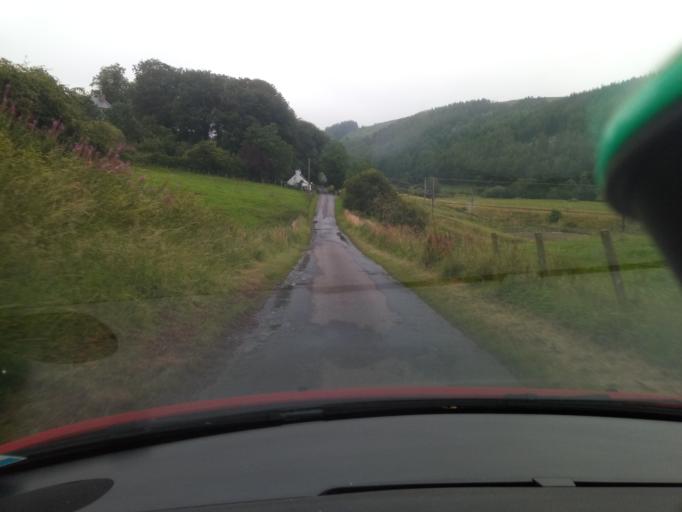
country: GB
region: Scotland
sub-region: The Scottish Borders
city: Galashiels
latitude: 55.7046
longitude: -2.8921
